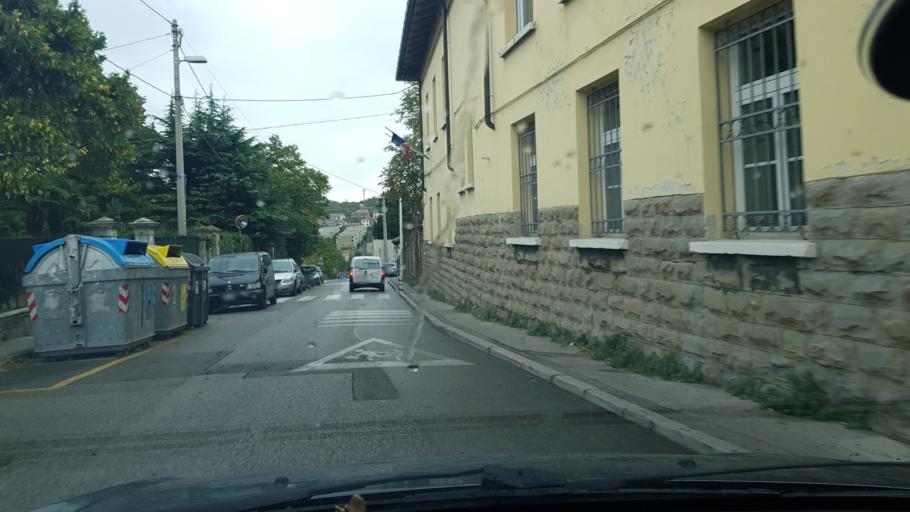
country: IT
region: Friuli Venezia Giulia
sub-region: Provincia di Trieste
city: Trieste
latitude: 45.6239
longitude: 13.7859
